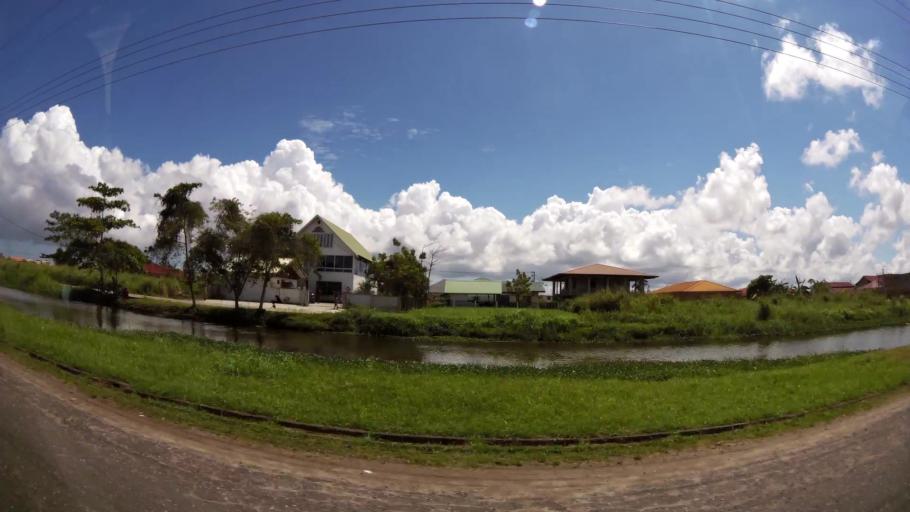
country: SR
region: Paramaribo
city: Paramaribo
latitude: 5.8646
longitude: -55.1387
